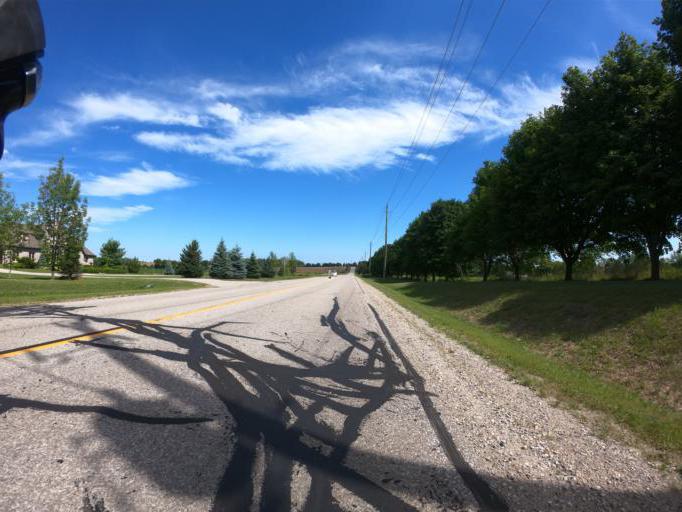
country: CA
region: Ontario
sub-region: Wellington County
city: Guelph
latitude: 43.5384
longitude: -80.3844
